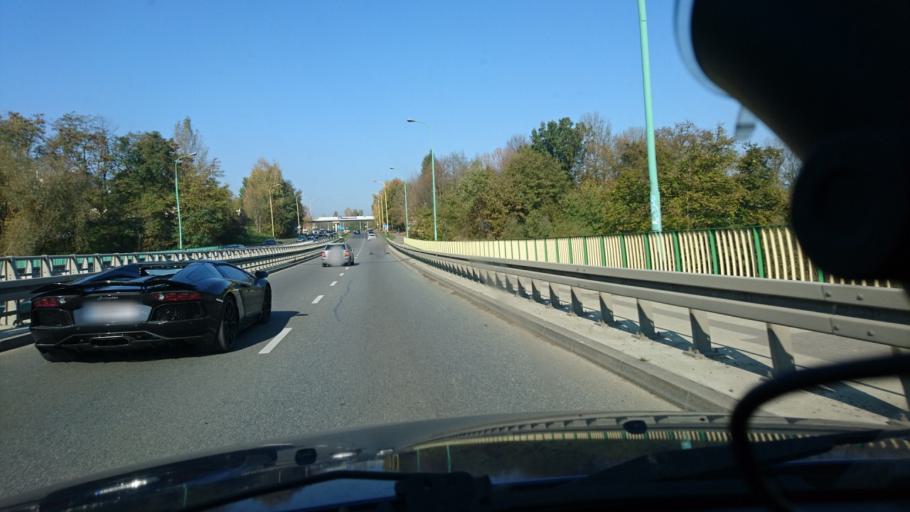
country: PL
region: Silesian Voivodeship
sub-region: Bielsko-Biala
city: Bielsko-Biala
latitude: 49.8066
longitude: 19.0299
